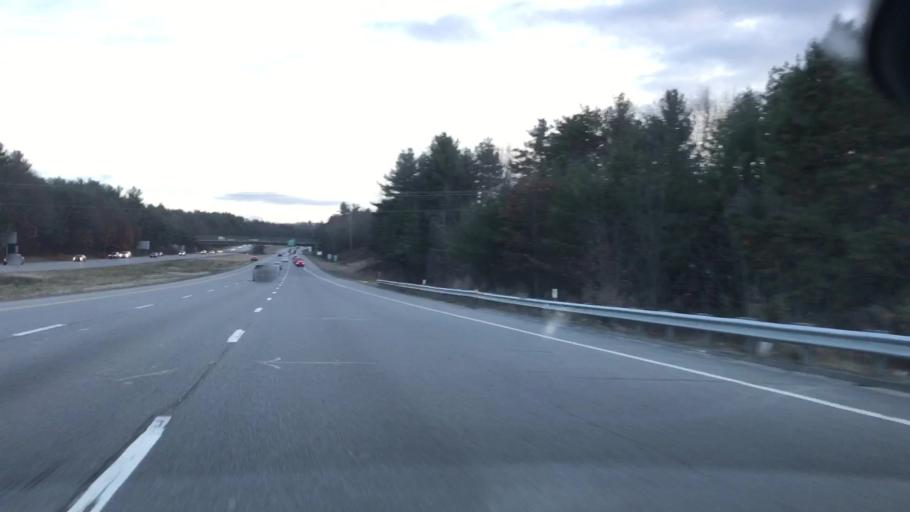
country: US
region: New Hampshire
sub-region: Merrimack County
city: South Hooksett
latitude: 43.0397
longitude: -71.4597
